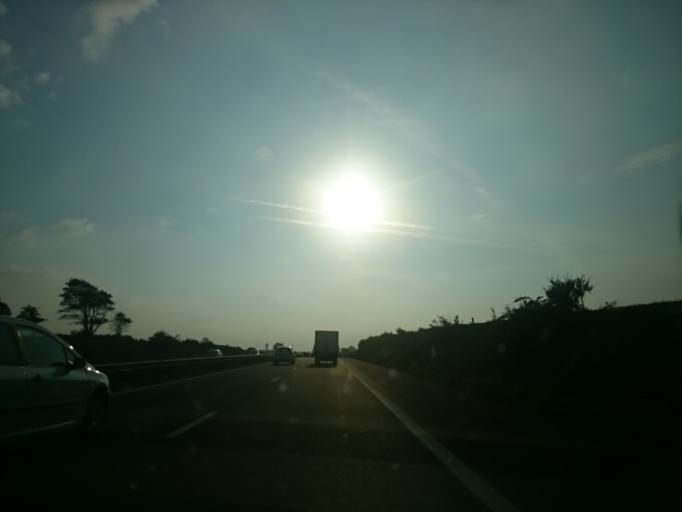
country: FR
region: Brittany
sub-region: Departement du Finistere
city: Saint-Thonan
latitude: 48.4779
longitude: -4.3118
